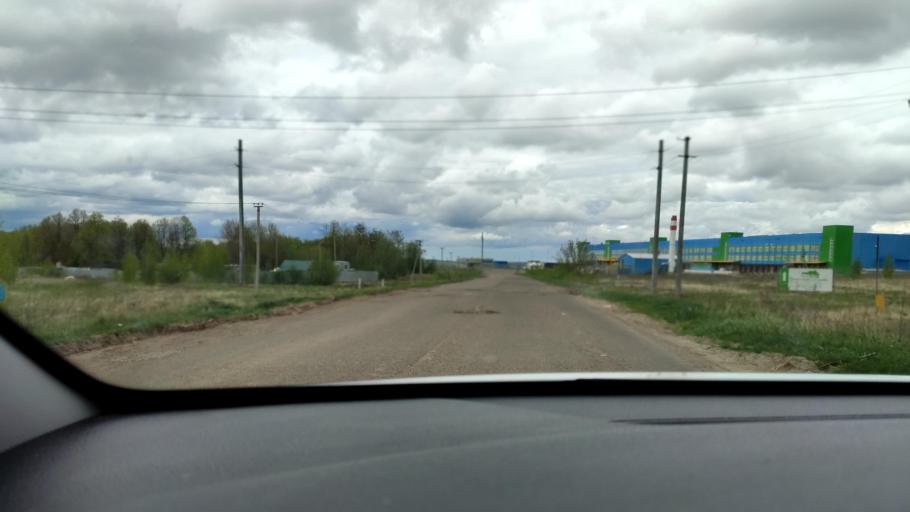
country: RU
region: Tatarstan
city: Vysokaya Gora
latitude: 55.8019
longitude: 49.3126
